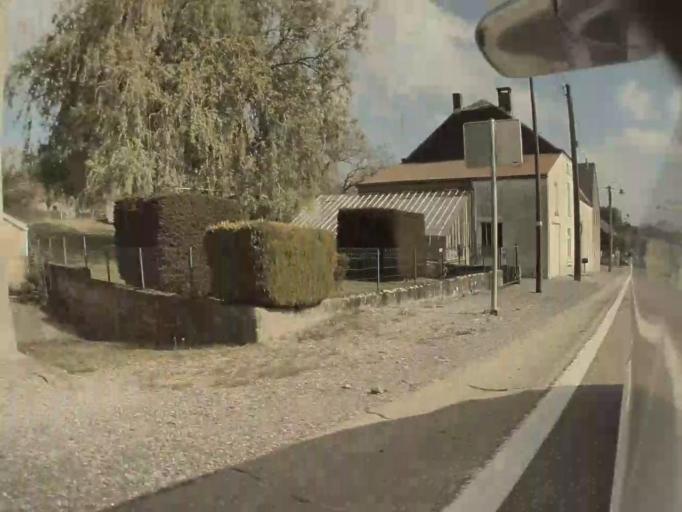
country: BE
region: Wallonia
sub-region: Province du Luxembourg
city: Tellin
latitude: 50.0797
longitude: 5.2155
